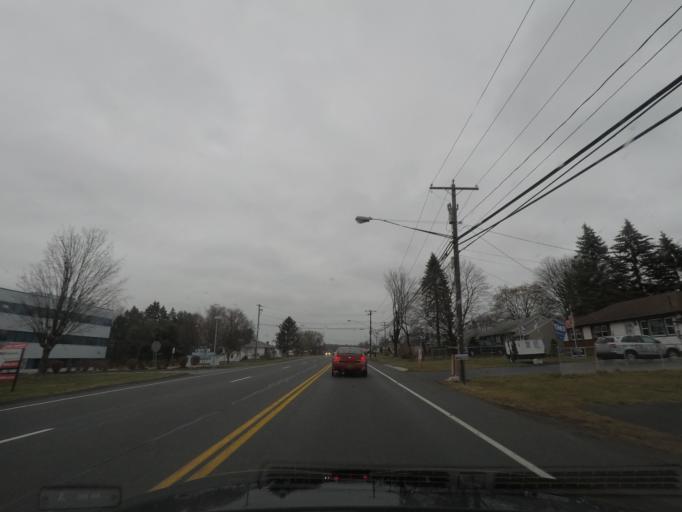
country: US
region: New York
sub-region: Rensselaer County
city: Hampton Manor
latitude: 42.6215
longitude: -73.7015
